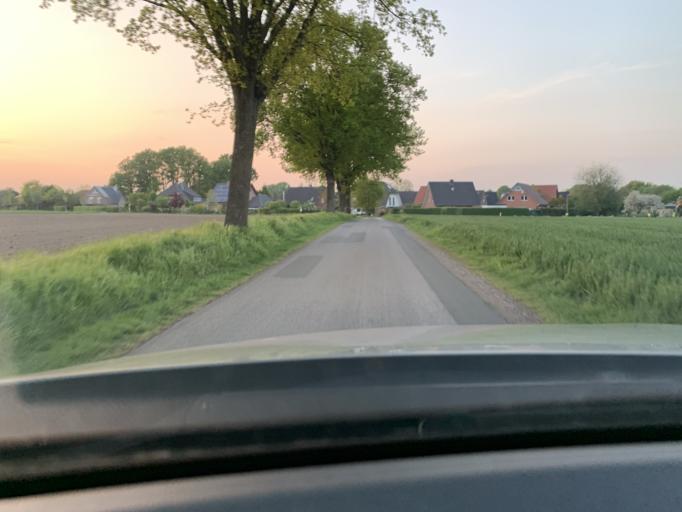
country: DE
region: North Rhine-Westphalia
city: Rietberg
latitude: 51.7978
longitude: 8.3832
